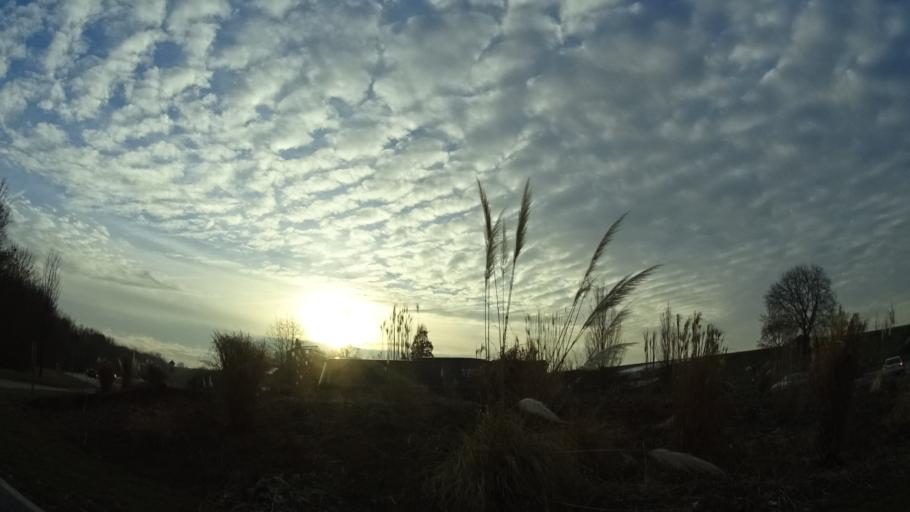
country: DE
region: Baden-Wuerttemberg
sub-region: Regierungsbezirk Stuttgart
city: Ditzingen
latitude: 48.8222
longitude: 9.0547
